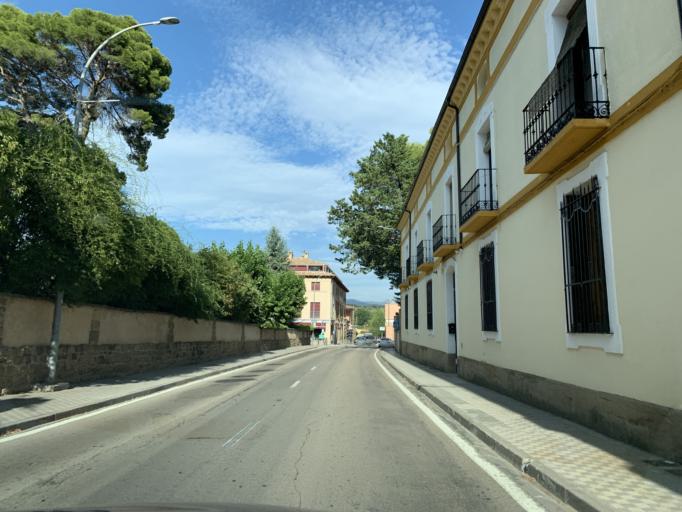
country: ES
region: Aragon
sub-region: Provincia de Huesca
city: Ayerbe
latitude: 42.2750
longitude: -0.6879
